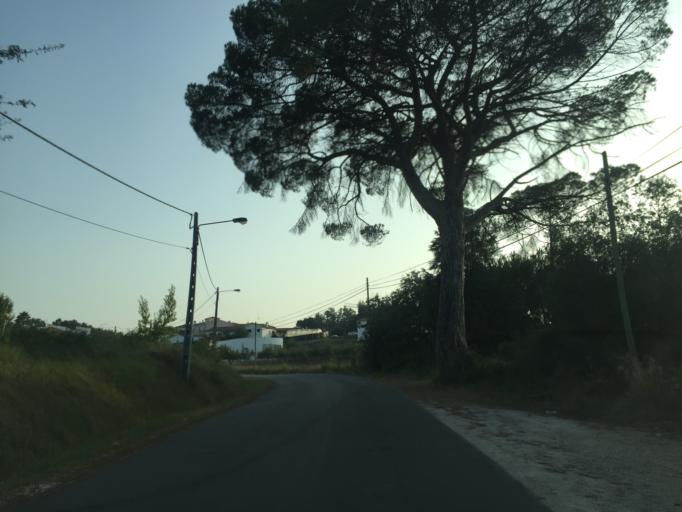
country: PT
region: Leiria
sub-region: Batalha
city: Batalha
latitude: 39.6561
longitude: -8.8334
